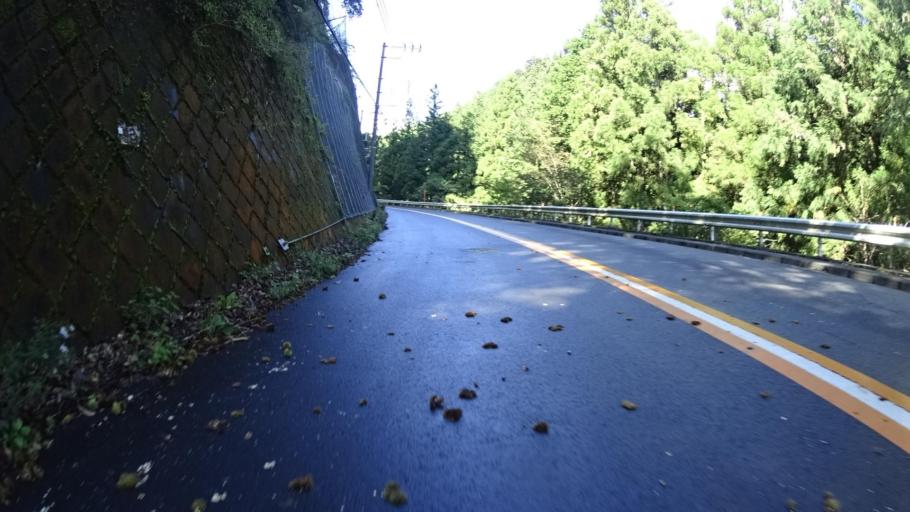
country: JP
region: Tokyo
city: Itsukaichi
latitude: 35.7344
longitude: 139.1183
